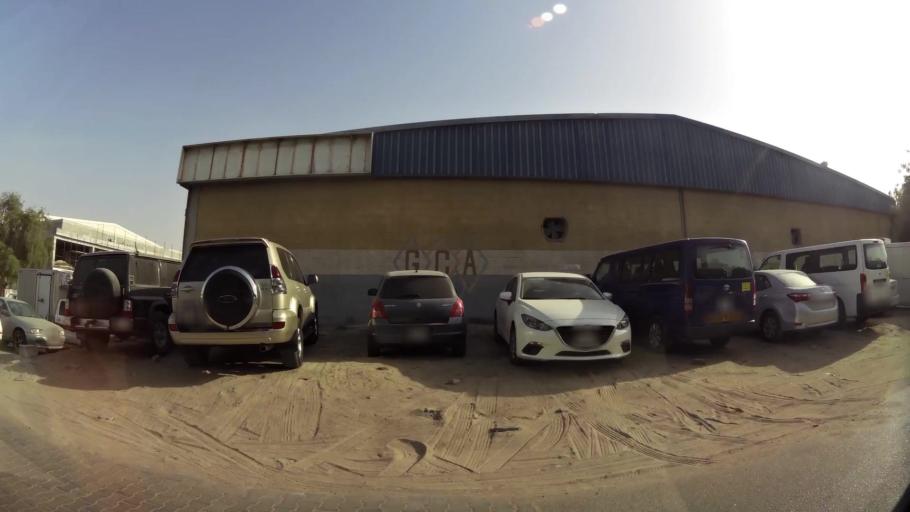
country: AE
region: Ash Shariqah
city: Sharjah
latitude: 25.2288
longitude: 55.3721
